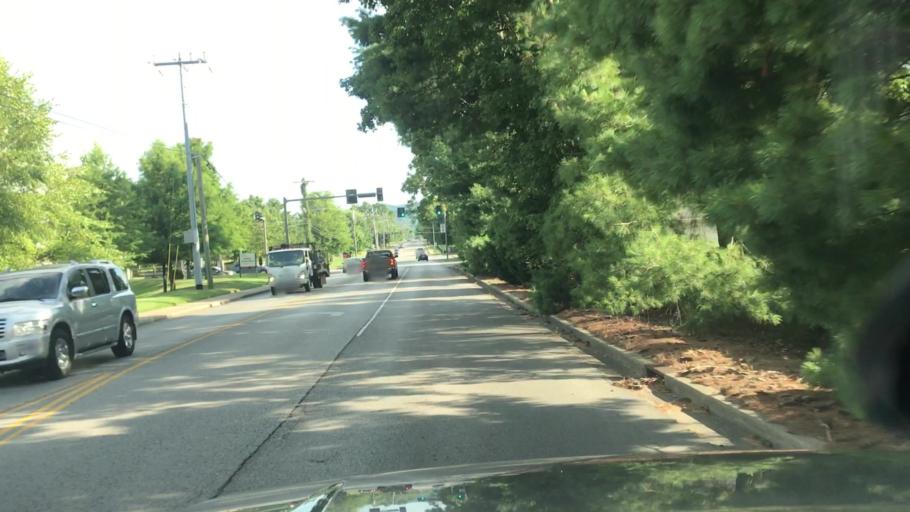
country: US
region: Tennessee
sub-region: Williamson County
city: Brentwood
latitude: 36.0378
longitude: -86.8168
